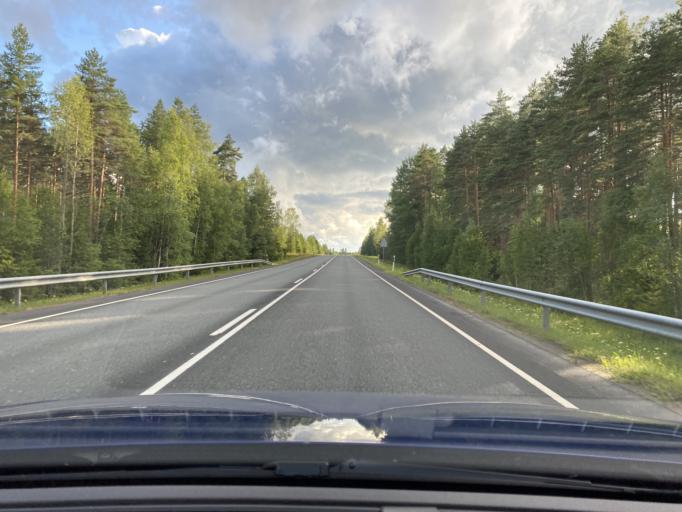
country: FI
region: Haeme
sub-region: Haemeenlinna
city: Renko
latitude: 60.8543
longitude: 24.1625
